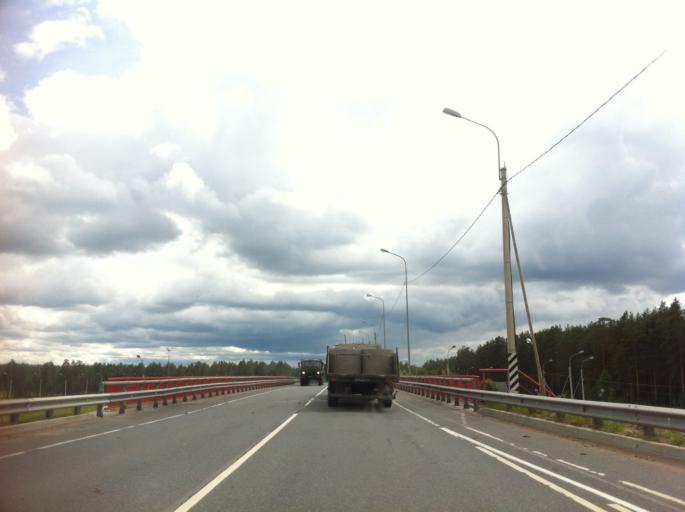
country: RU
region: Leningrad
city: Luga
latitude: 58.7316
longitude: 29.8835
